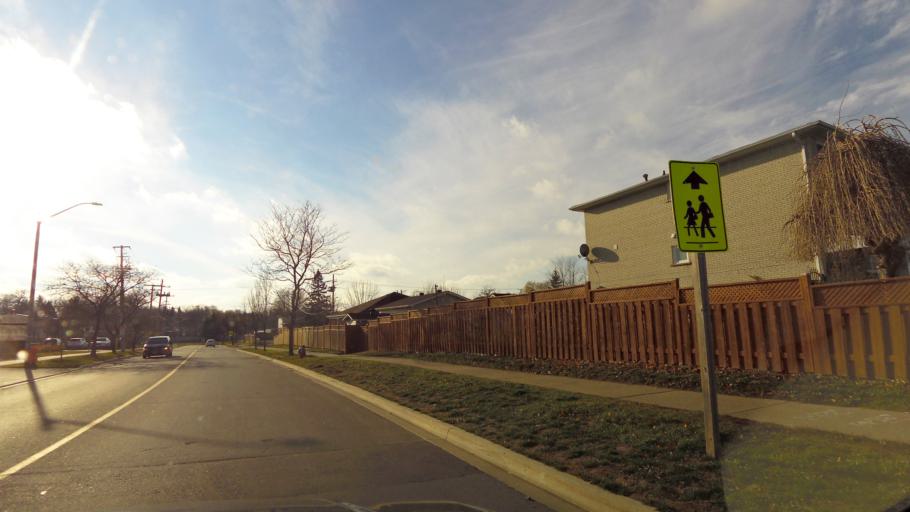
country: CA
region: Ontario
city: Mississauga
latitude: 43.5601
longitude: -79.6559
